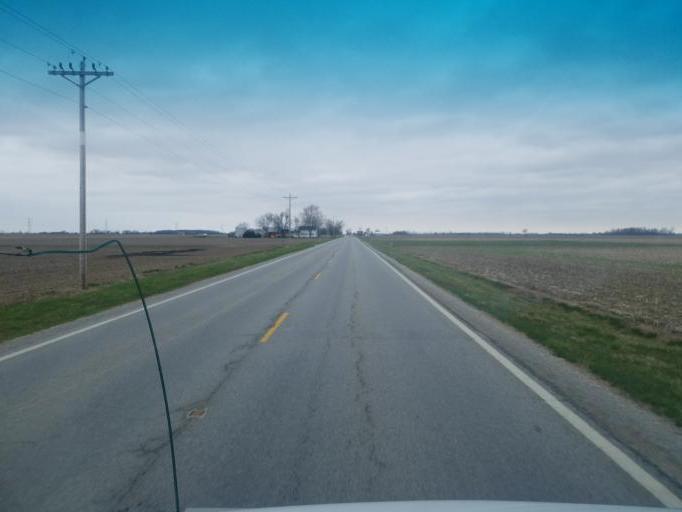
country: US
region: Ohio
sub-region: Allen County
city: Delphos
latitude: 40.9321
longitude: -84.4023
